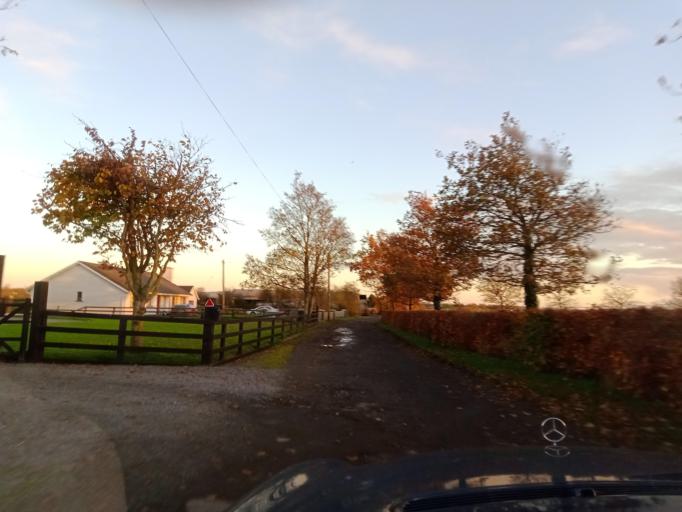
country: IE
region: Leinster
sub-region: Kilkenny
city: Kilkenny
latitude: 52.6034
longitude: -7.1912
